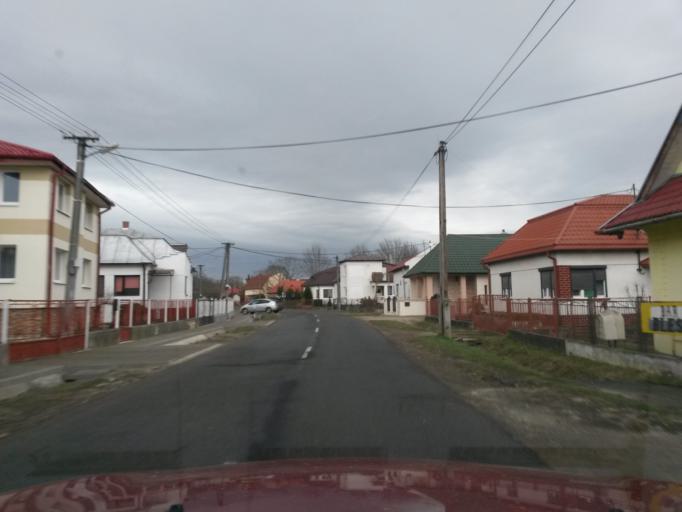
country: SK
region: Kosicky
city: Michalovce
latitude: 48.6645
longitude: 22.0260
